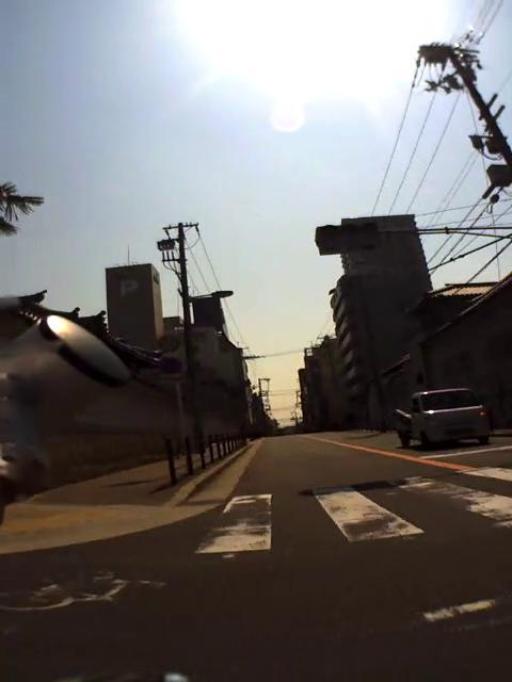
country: JP
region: Osaka
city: Osaka-shi
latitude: 34.6697
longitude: 135.5162
